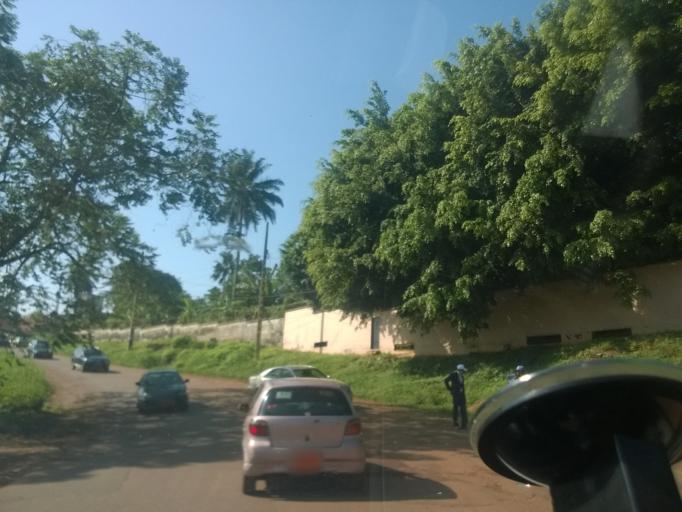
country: CM
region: Centre
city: Yaounde
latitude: 3.8564
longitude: 11.5110
